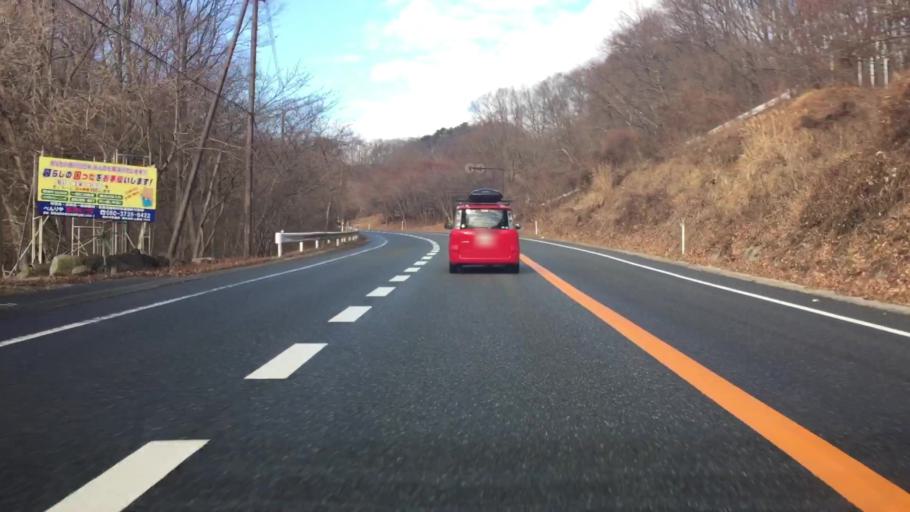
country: JP
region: Nagano
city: Saku
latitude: 36.3025
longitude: 138.6713
